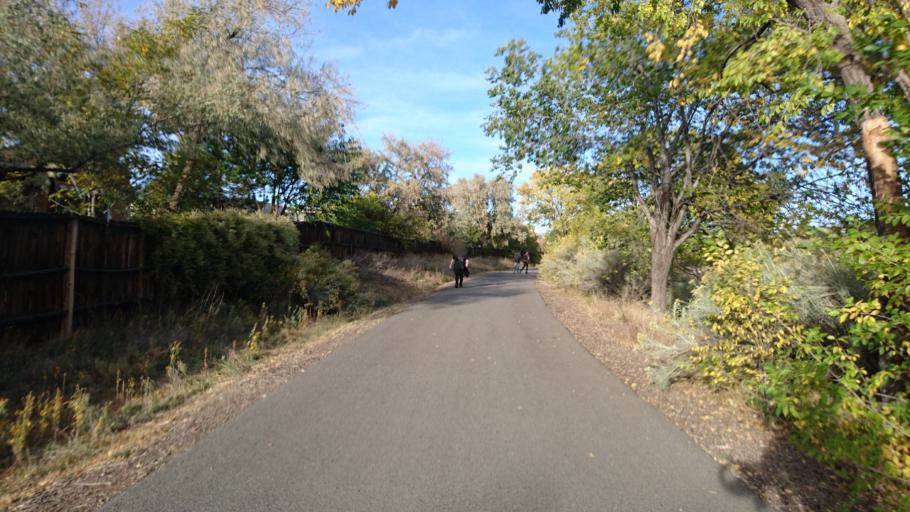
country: US
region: New Mexico
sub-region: Santa Fe County
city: Agua Fria
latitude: 35.6439
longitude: -105.9806
